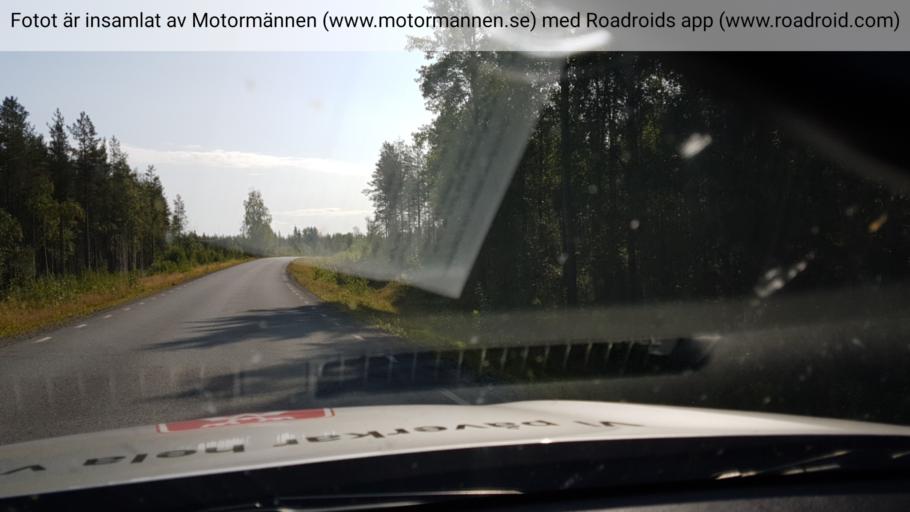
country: SE
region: Norrbotten
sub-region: Alvsbyns Kommun
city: AElvsbyn
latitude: 65.5930
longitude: 20.7666
